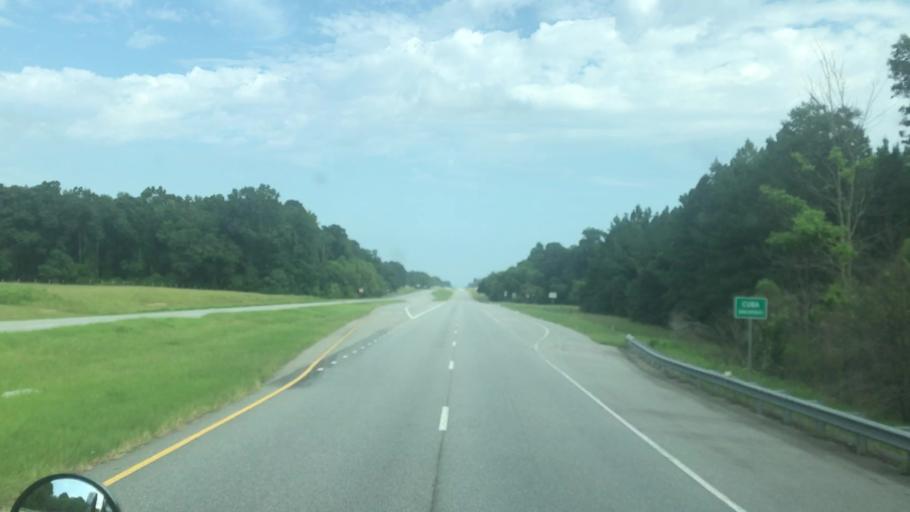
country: US
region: Georgia
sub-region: Early County
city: Blakely
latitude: 31.2989
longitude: -84.8580
